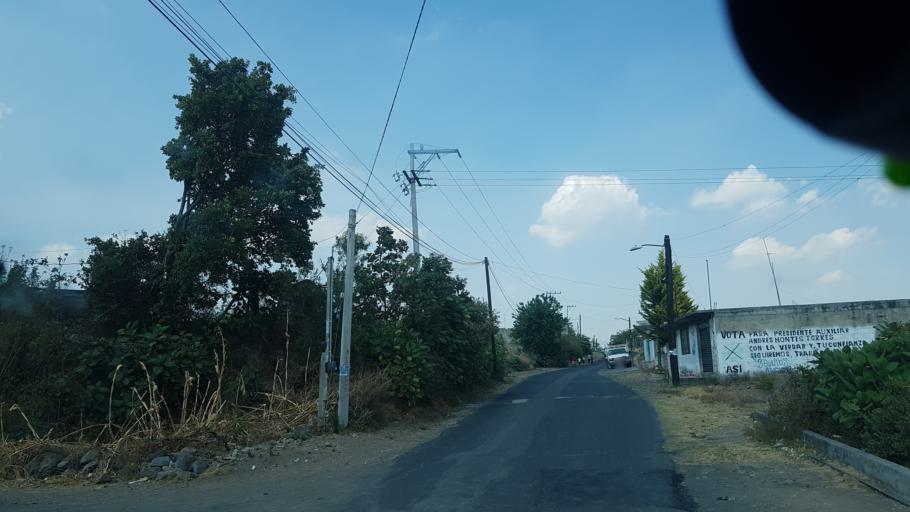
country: MX
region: Puebla
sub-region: Atlixco
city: San Pedro Benito Juarez
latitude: 18.9513
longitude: -98.5458
